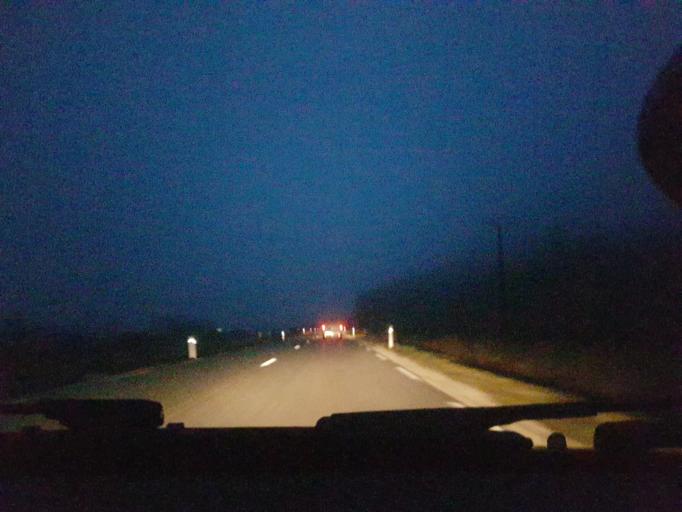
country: FR
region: Franche-Comte
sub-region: Departement du Doubs
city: Doubs
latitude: 46.9482
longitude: 6.3425
